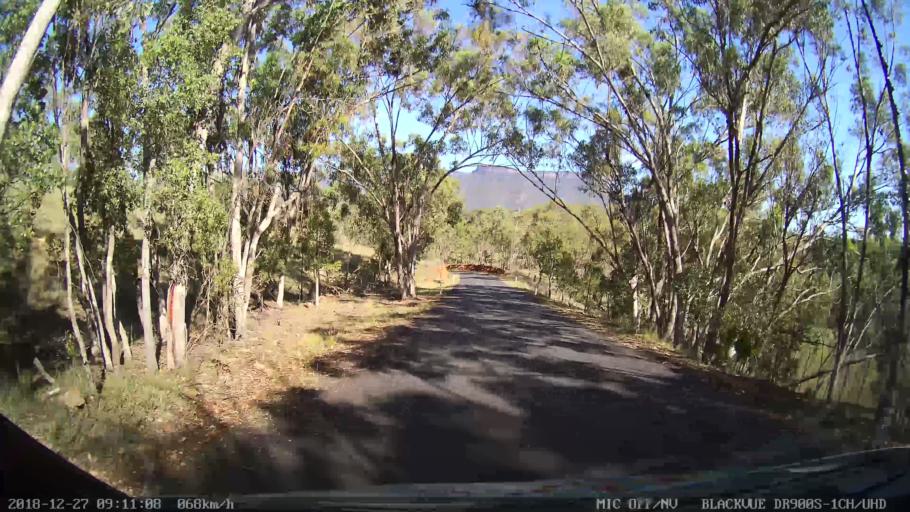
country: AU
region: New South Wales
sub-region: Lithgow
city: Portland
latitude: -33.1357
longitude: 150.1170
